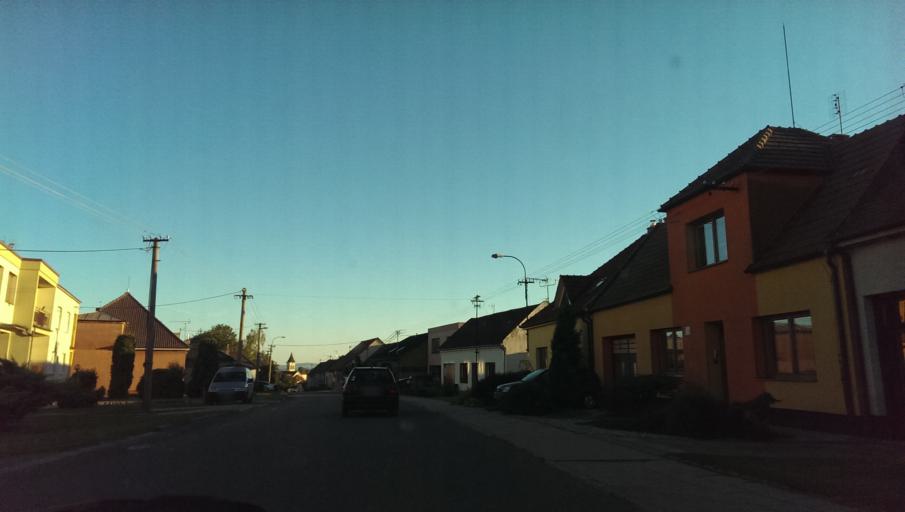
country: CZ
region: Zlin
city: Zlechov
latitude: 49.0771
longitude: 17.3779
